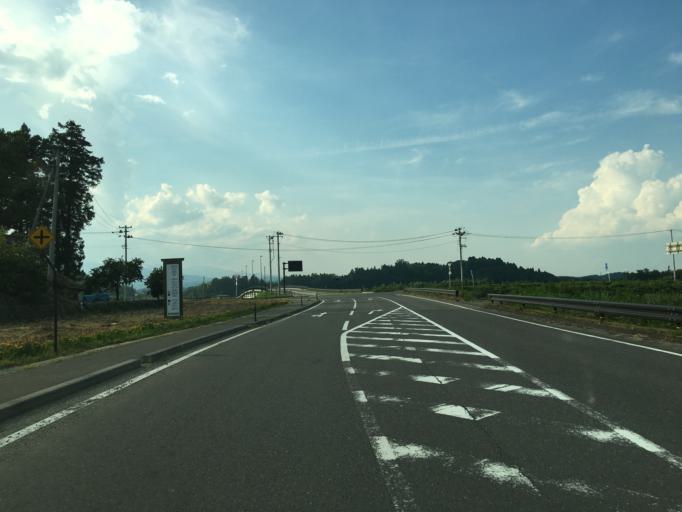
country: JP
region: Fukushima
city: Nihommatsu
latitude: 37.5519
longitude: 140.4370
